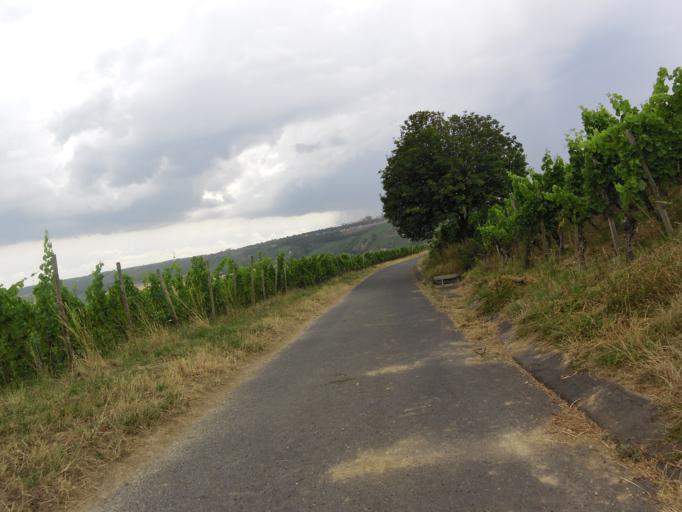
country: DE
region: Bavaria
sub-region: Regierungsbezirk Unterfranken
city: Randersacker
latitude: 49.7632
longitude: 9.9793
